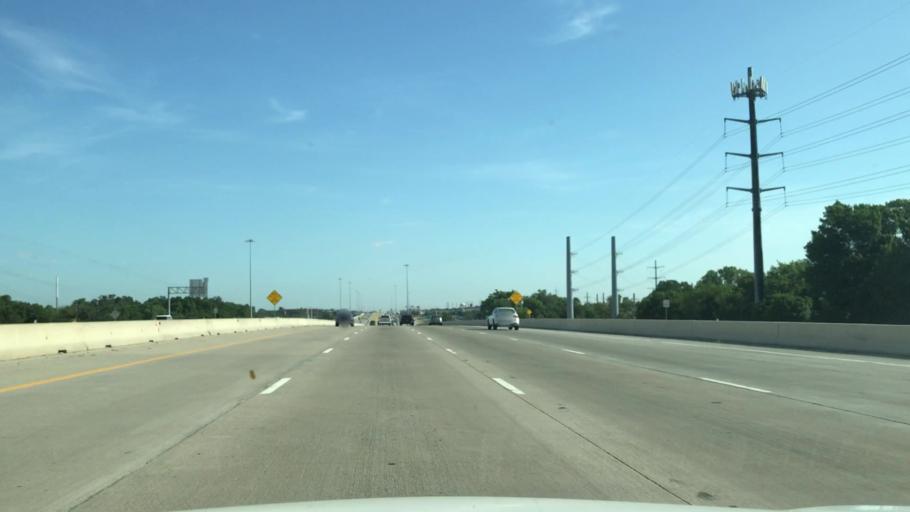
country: US
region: Texas
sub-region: Collin County
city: Fairview
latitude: 33.1822
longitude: -96.6397
